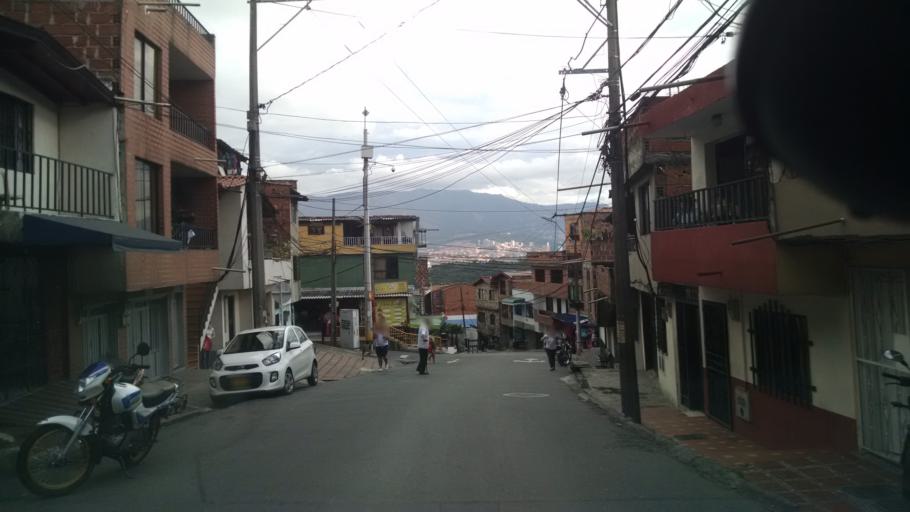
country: CO
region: Antioquia
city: Medellin
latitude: 6.2824
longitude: -75.5905
